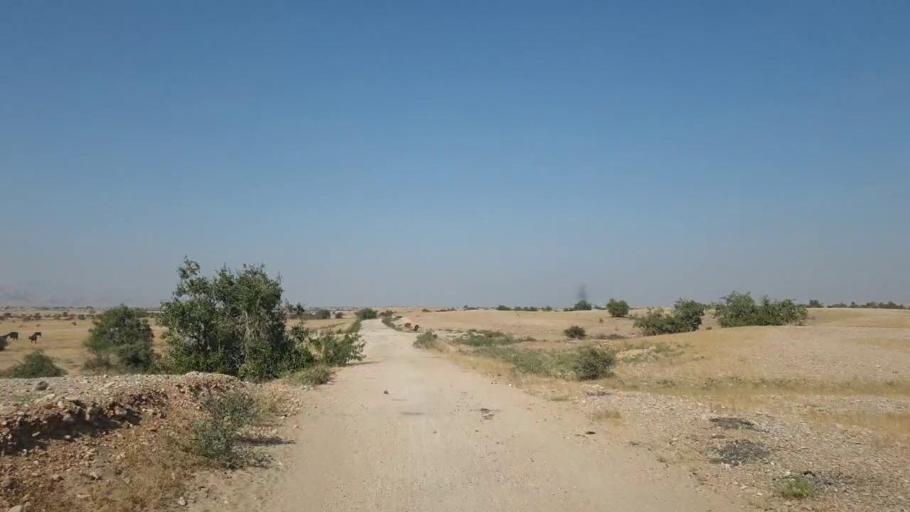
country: PK
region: Sindh
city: Jamshoro
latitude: 25.4888
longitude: 67.8394
